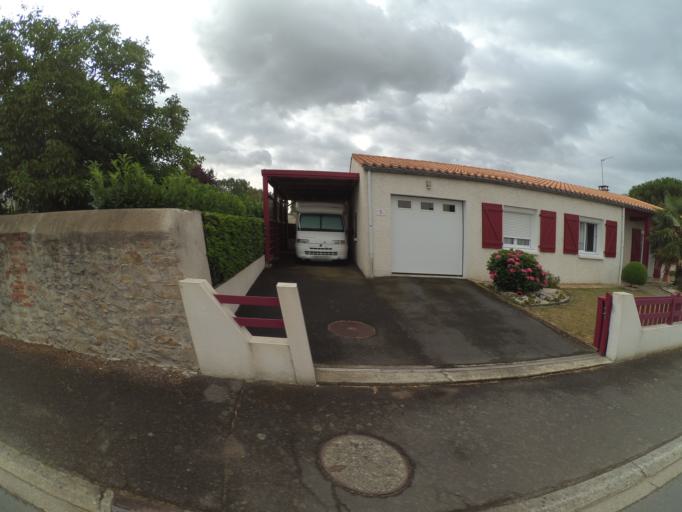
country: FR
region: Pays de la Loire
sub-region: Departement de la Vendee
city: Cugand
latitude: 47.0604
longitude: -1.2568
